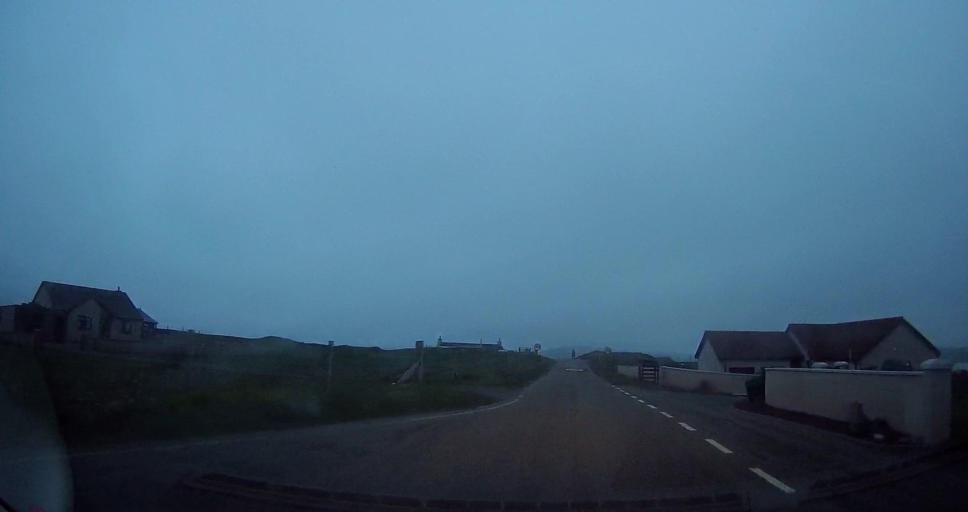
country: GB
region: Scotland
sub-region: Shetland Islands
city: Sandwick
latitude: 60.0151
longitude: -1.2281
